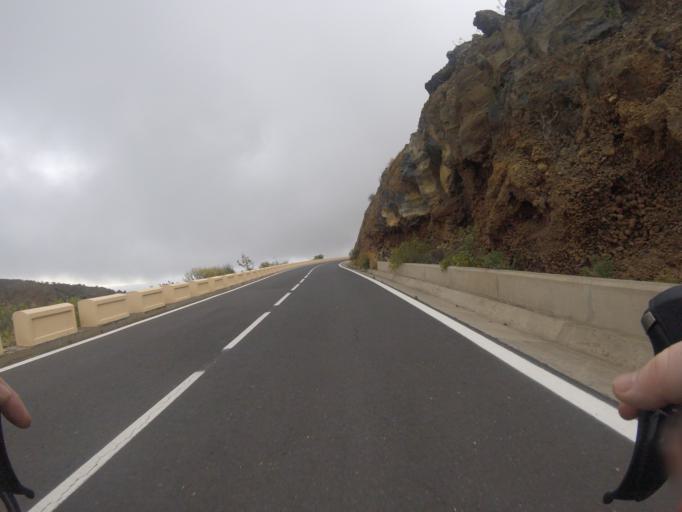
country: ES
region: Canary Islands
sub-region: Provincia de Santa Cruz de Tenerife
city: Lomo de Arico
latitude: 28.1887
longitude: -16.4804
